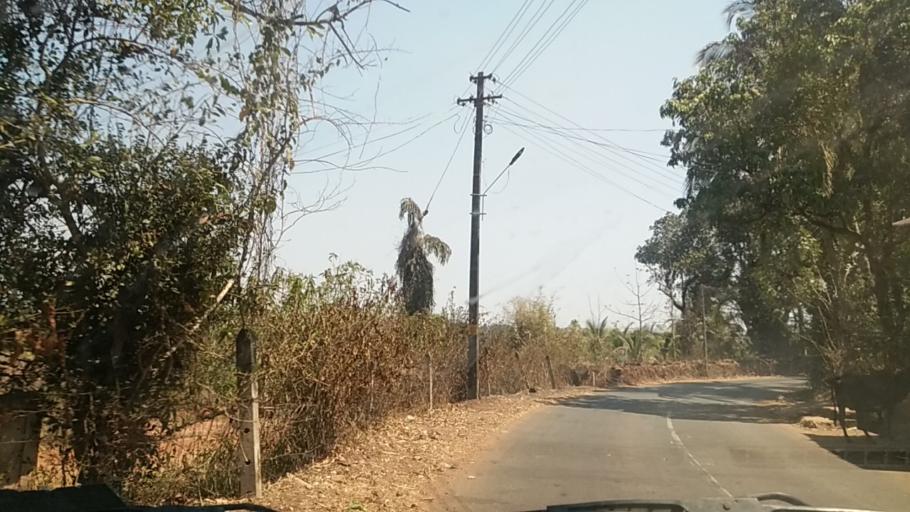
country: IN
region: Goa
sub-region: North Goa
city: Dicholi
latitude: 15.5773
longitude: 73.9158
